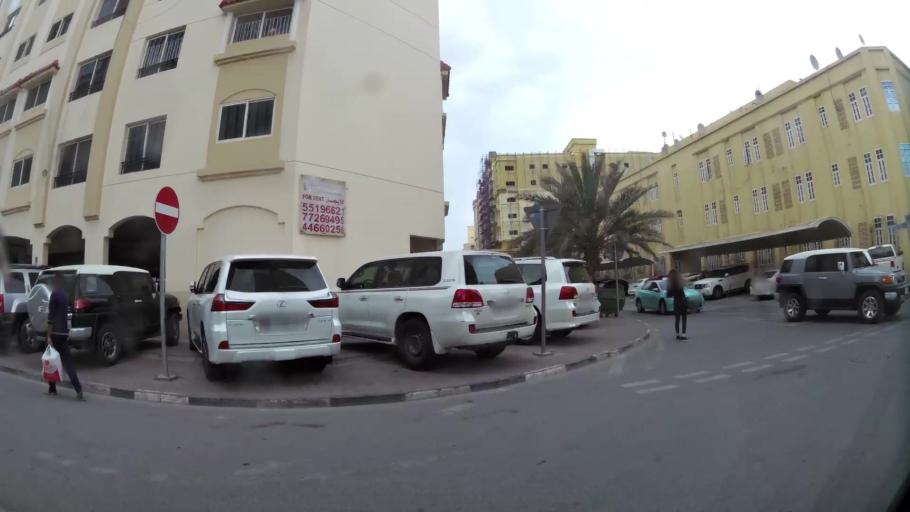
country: QA
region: Baladiyat ad Dawhah
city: Doha
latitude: 25.2806
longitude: 51.5082
